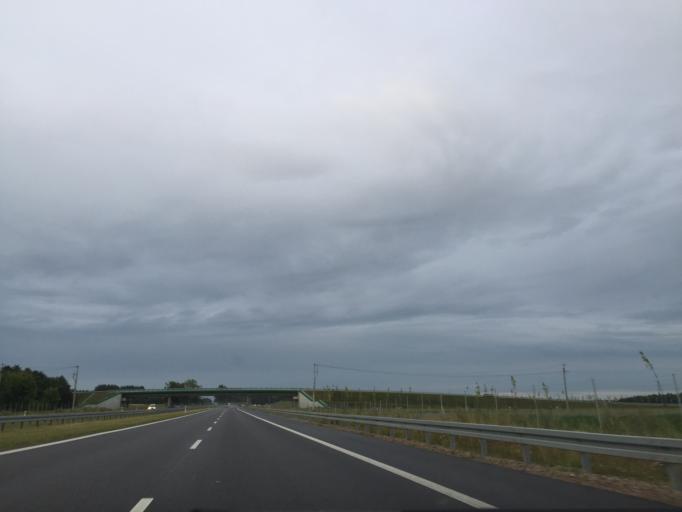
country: PL
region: Podlasie
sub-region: Powiat zambrowski
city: Rutki-Kossaki
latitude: 53.0788
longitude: 22.4424
